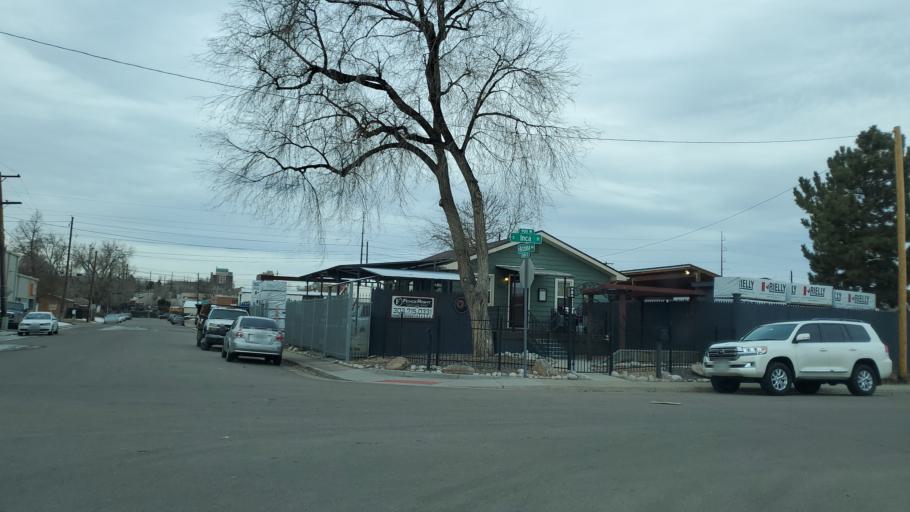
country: US
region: Colorado
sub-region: Denver County
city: Denver
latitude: 39.6949
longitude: -104.9979
